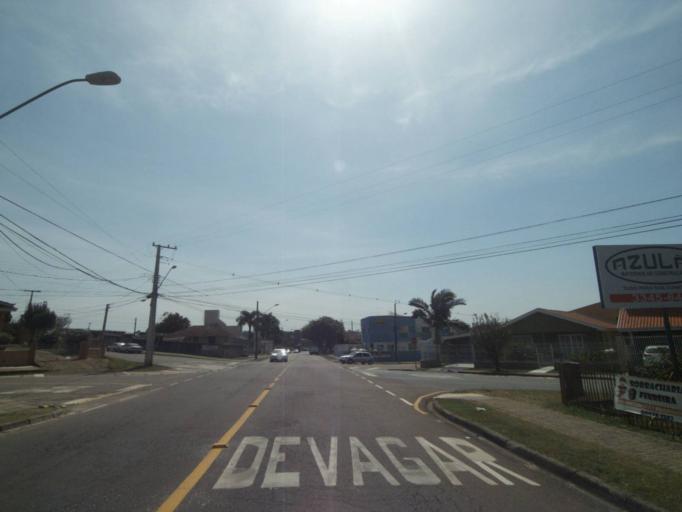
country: BR
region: Parana
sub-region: Curitiba
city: Curitiba
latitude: -25.4682
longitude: -49.3070
